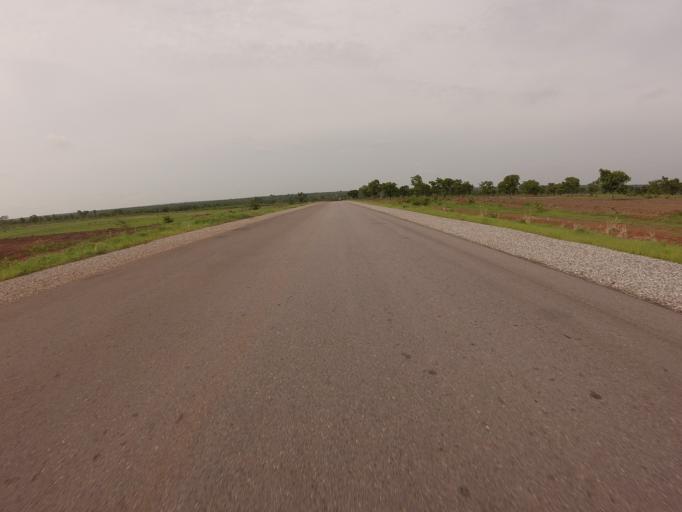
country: GH
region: Northern
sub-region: Yendi
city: Yendi
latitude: 9.8033
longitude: -0.1132
